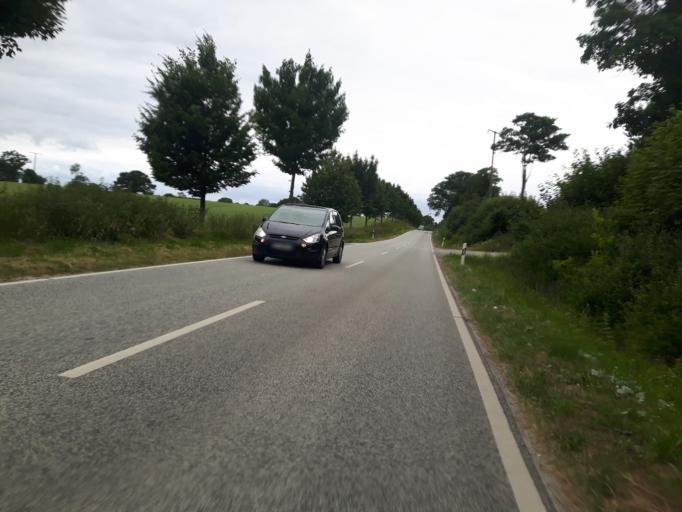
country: DE
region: Schleswig-Holstein
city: Gromitz
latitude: 54.1401
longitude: 10.9374
